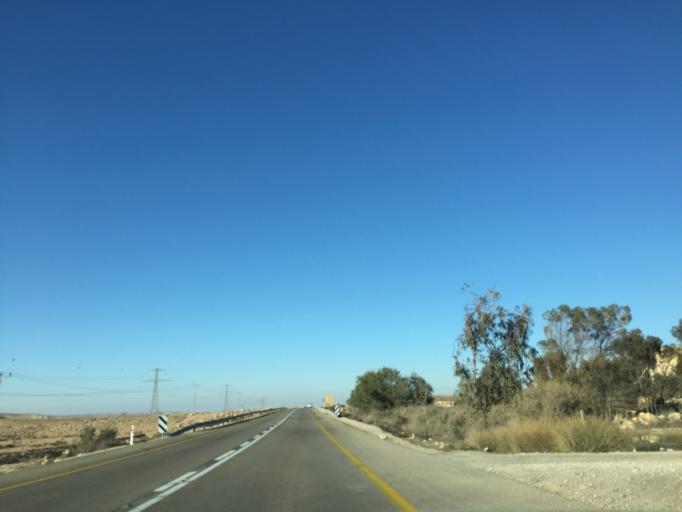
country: IL
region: Southern District
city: Midreshet Ben-Gurion
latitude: 30.7846
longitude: 34.7685
